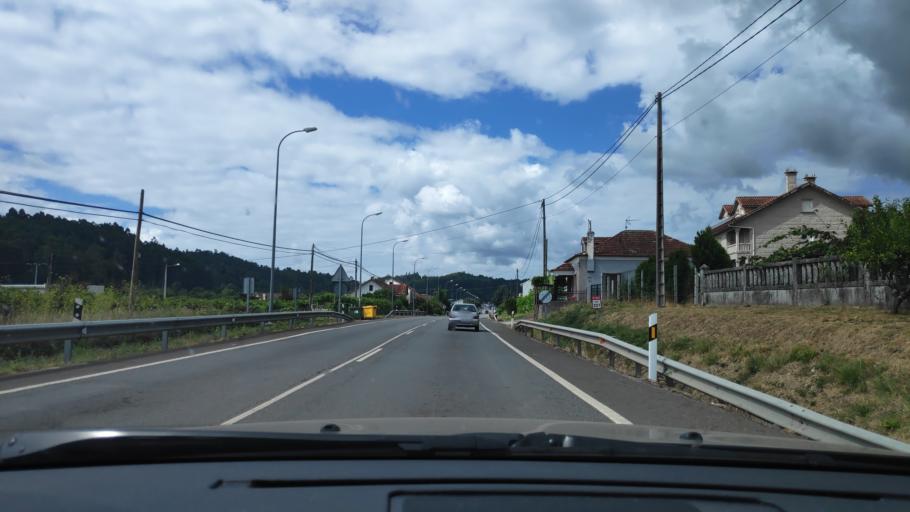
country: ES
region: Galicia
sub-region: Provincia de Pontevedra
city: Portas
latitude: 42.6011
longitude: -8.6586
